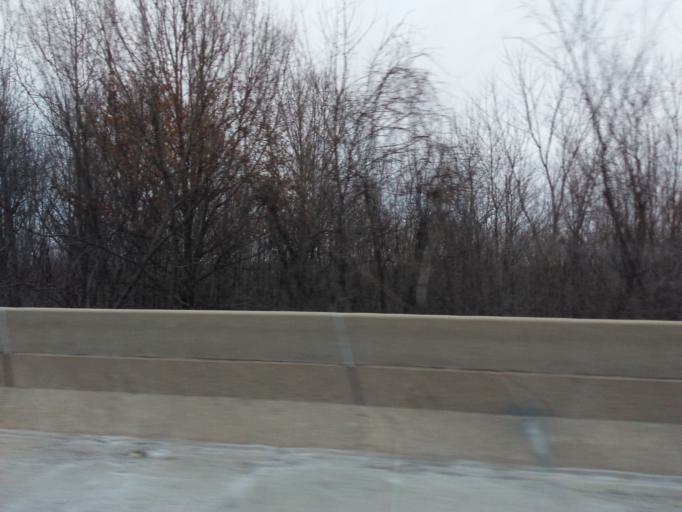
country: US
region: Illinois
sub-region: Washington County
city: Okawville
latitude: 38.4767
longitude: -89.5786
